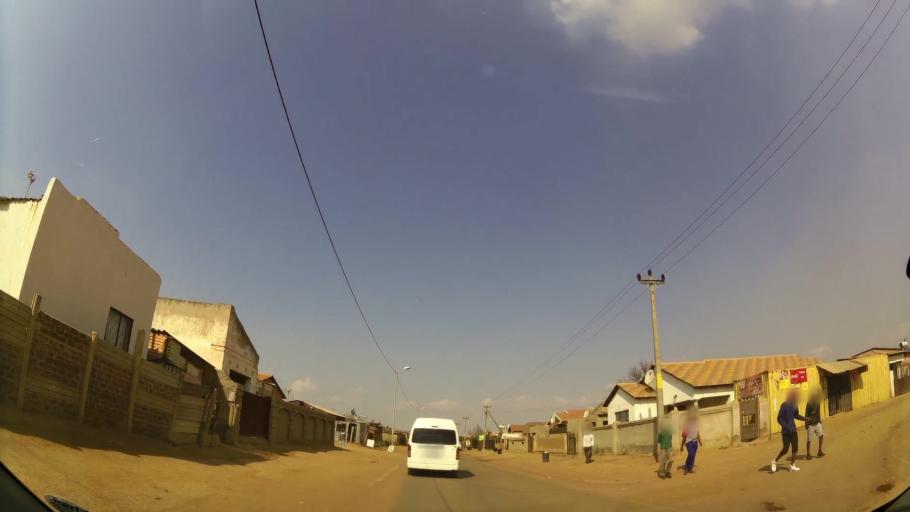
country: ZA
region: Gauteng
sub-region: Ekurhuleni Metropolitan Municipality
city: Springs
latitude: -26.1105
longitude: 28.4850
